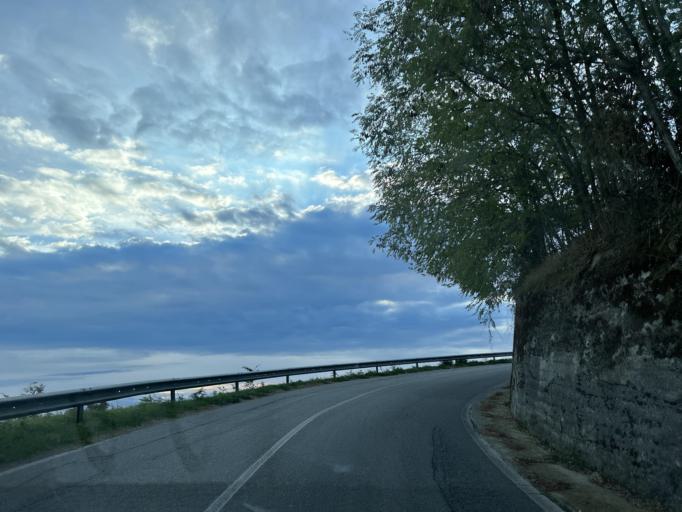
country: IT
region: Calabria
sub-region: Provincia di Catanzaro
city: Gasperina
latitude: 38.7440
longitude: 16.5077
